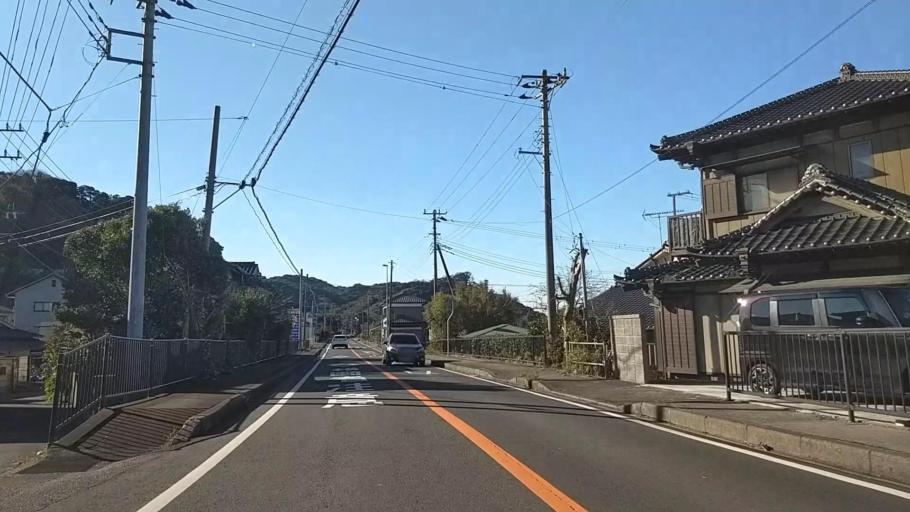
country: JP
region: Chiba
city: Futtsu
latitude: 35.2025
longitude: 139.8315
